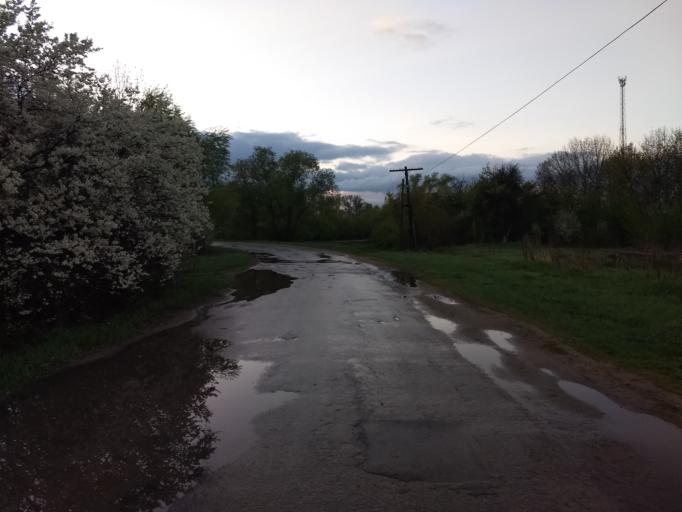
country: RU
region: Lipetsk
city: Zadonsk
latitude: 52.2919
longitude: 38.9500
